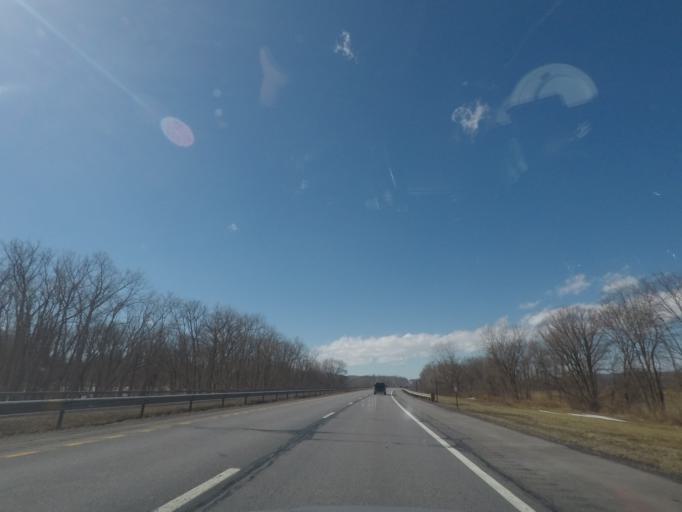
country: US
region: New York
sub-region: Montgomery County
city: Tribes Hill
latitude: 42.9303
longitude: -74.3079
